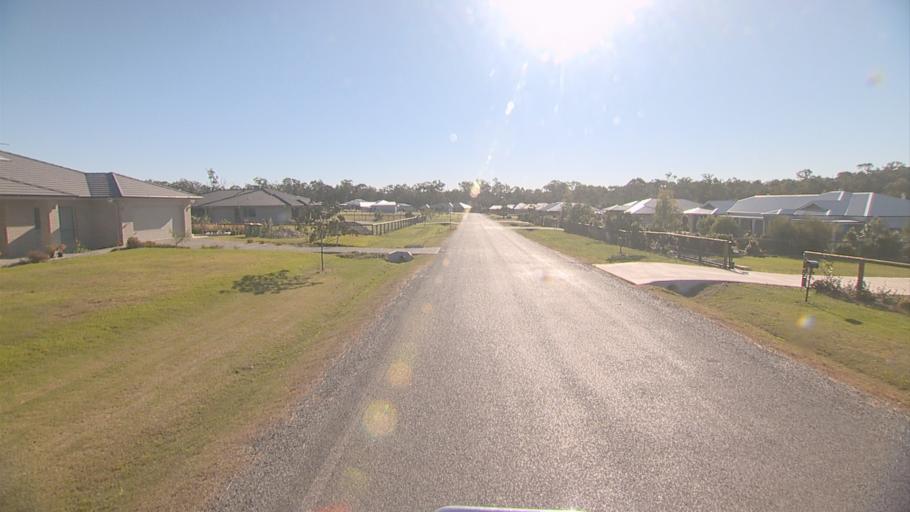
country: AU
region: Queensland
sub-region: Logan
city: Logan Reserve
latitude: -27.7498
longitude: 153.1352
